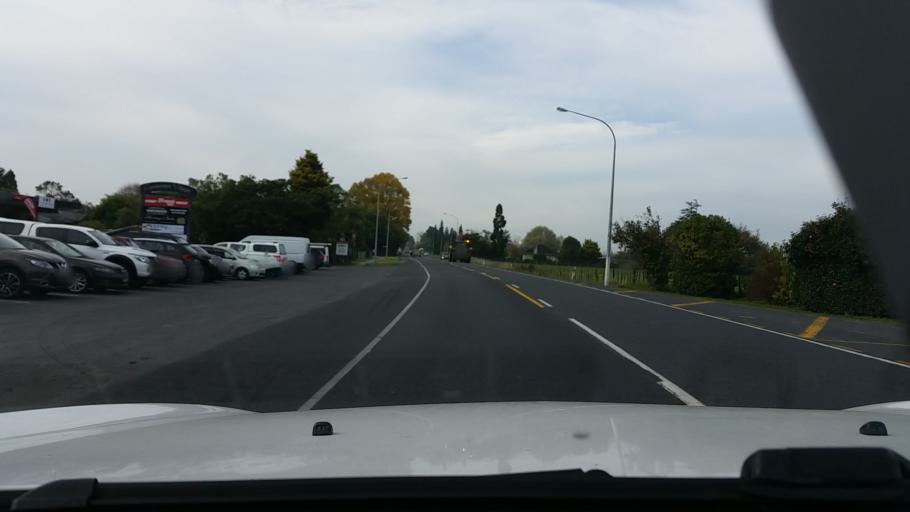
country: NZ
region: Waikato
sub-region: Hamilton City
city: Hamilton
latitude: -37.6696
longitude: 175.3033
